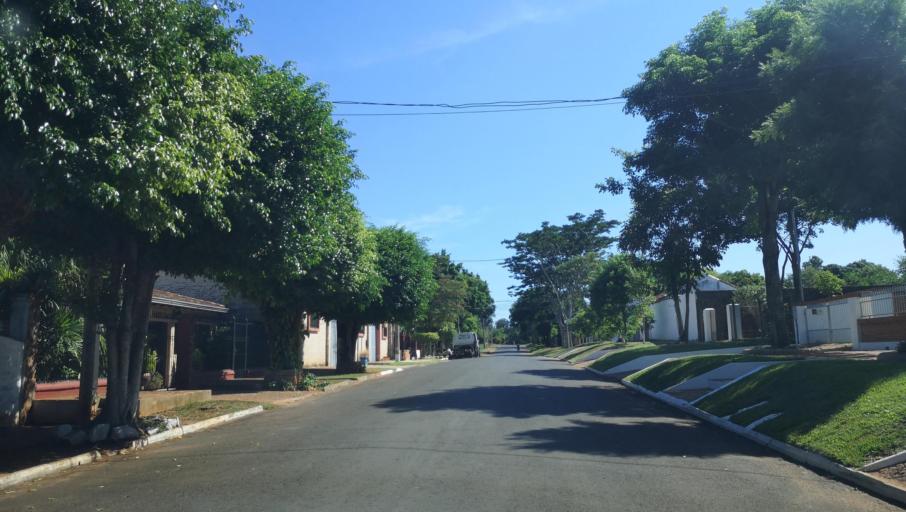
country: PY
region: Misiones
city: Santa Maria
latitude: -26.8931
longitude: -57.0253
